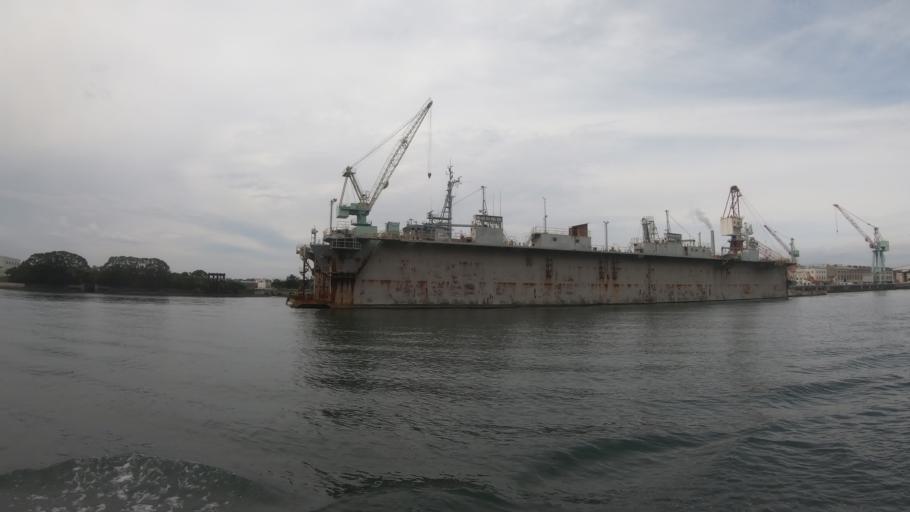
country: JP
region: Kanagawa
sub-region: Kawasaki-shi
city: Kawasaki
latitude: 35.4883
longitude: 139.6921
